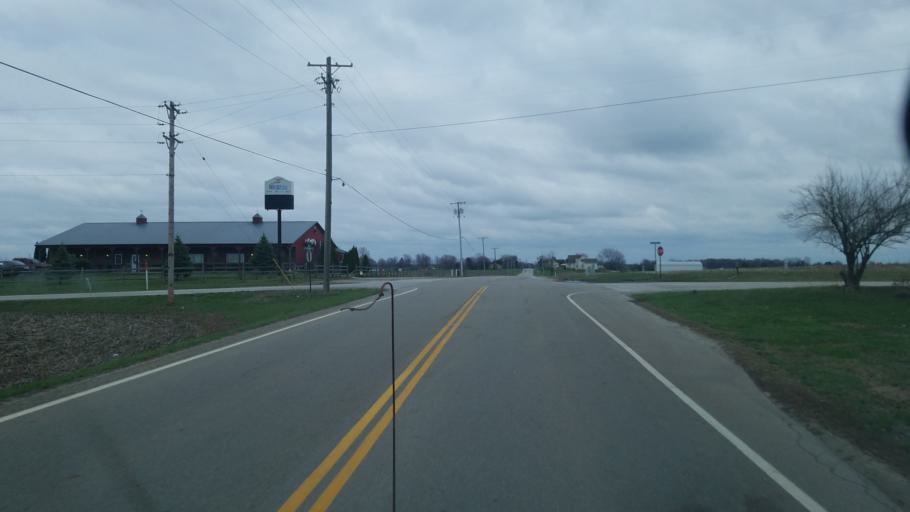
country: US
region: Ohio
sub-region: Fayette County
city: Washington Court House
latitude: 39.5487
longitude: -83.4799
